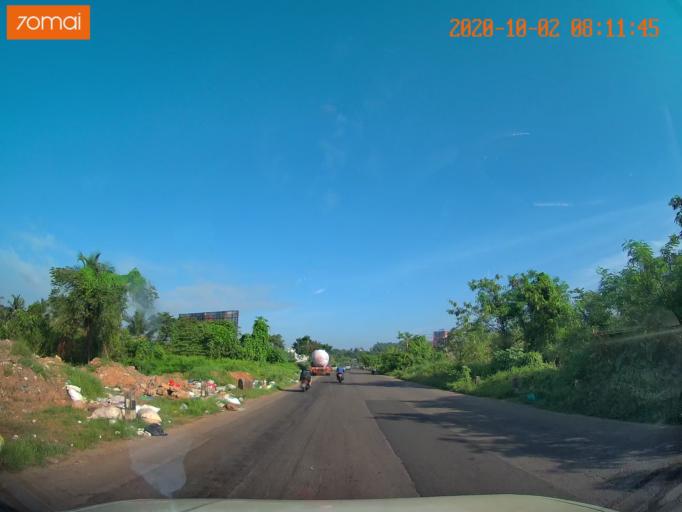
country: IN
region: Kerala
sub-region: Kozhikode
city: Kozhikode
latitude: 11.2768
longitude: 75.8064
